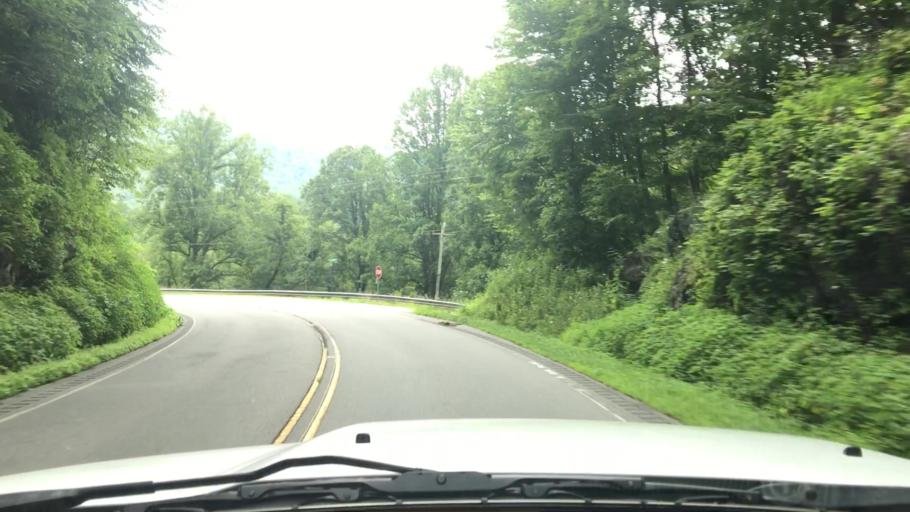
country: US
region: North Carolina
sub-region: Graham County
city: Robbinsville
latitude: 35.2728
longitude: -83.6911
